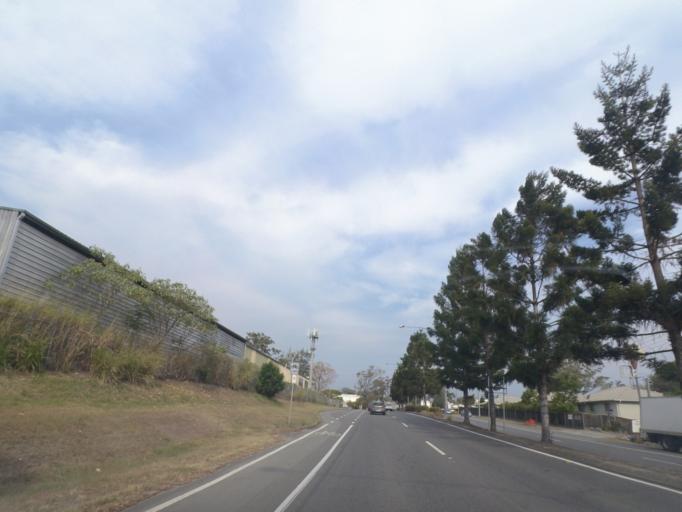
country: AU
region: Queensland
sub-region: Brisbane
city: Sunnybank
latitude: -27.5980
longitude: 153.0336
